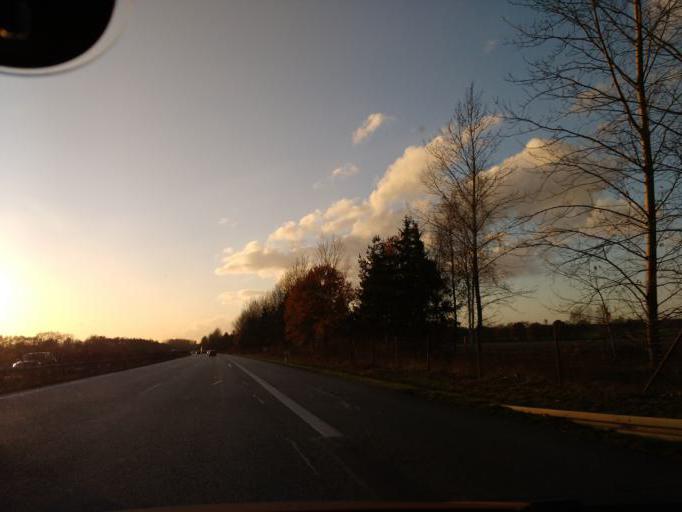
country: DE
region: Mecklenburg-Vorpommern
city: Hagenow
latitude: 53.4878
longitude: 11.2372
